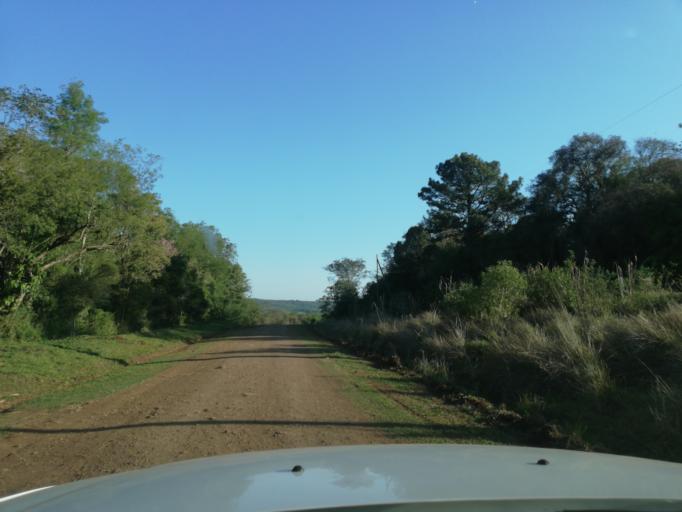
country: AR
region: Misiones
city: Cerro Cora
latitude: -27.5851
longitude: -55.6880
